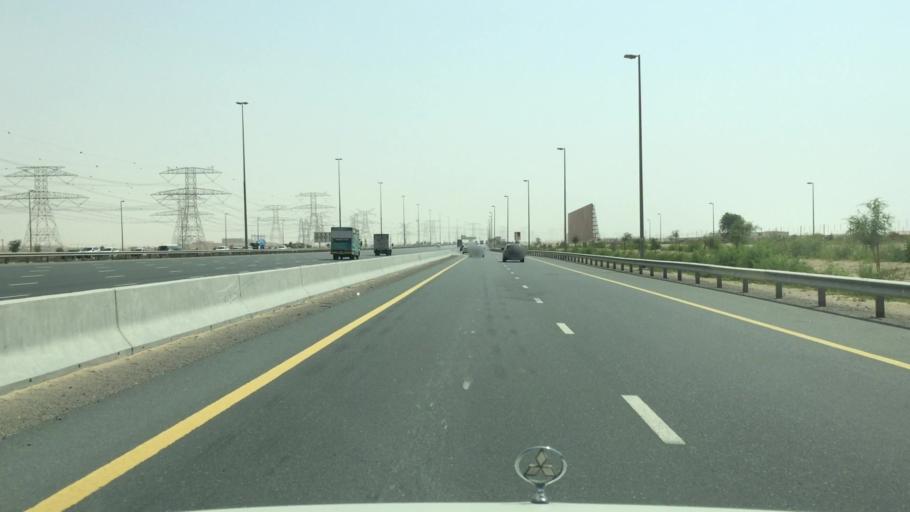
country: AE
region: Dubai
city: Dubai
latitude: 25.0835
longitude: 55.3859
